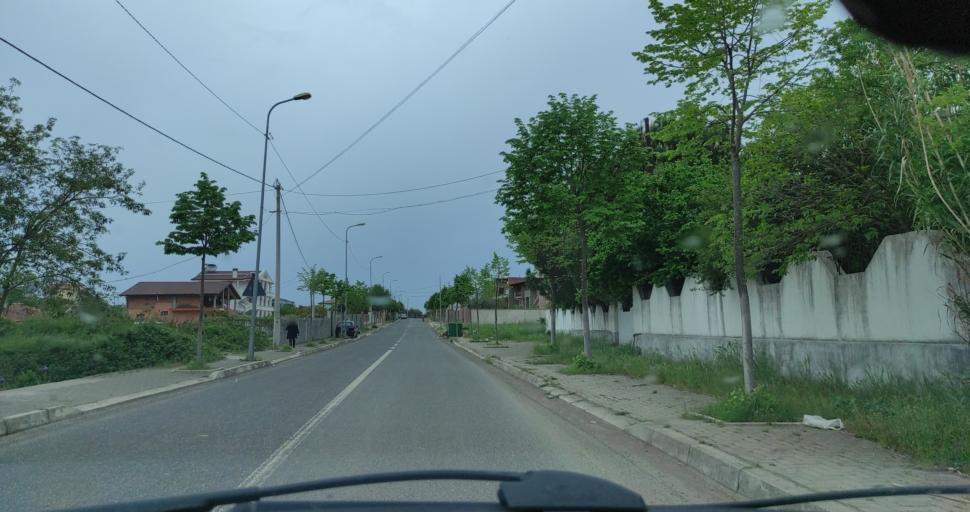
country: AL
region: Lezhe
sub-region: Rrethi i Kurbinit
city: Mamurras
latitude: 41.5848
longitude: 19.6931
